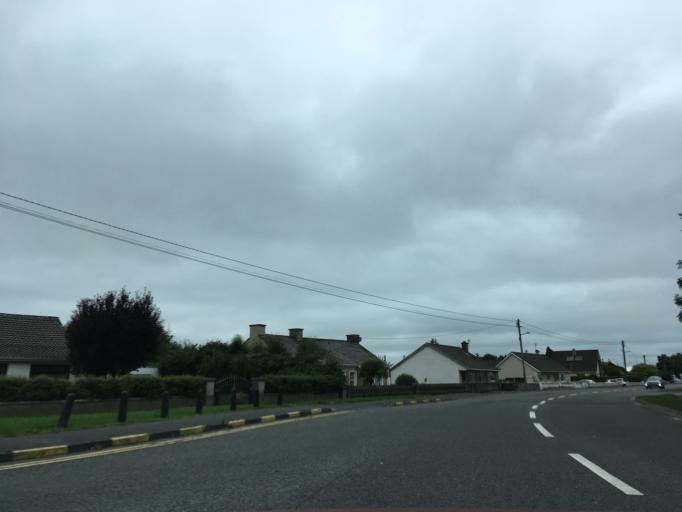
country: IE
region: Munster
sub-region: An Clar
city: Ennis
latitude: 52.8313
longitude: -8.9921
